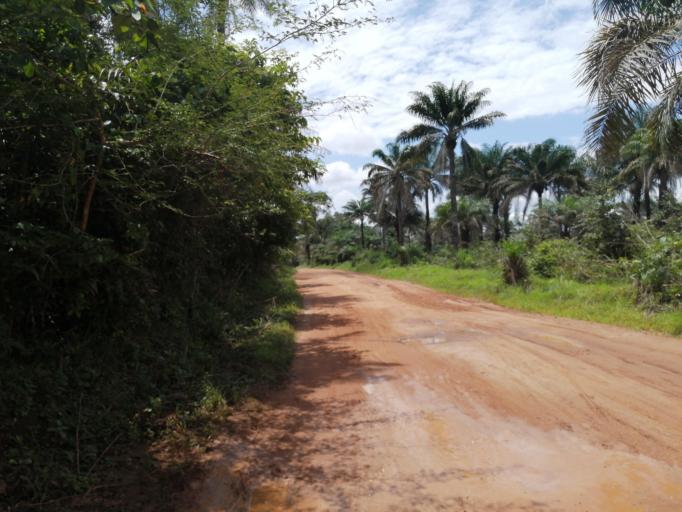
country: SL
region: Northern Province
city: Konakridee
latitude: 8.7454
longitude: -13.1457
